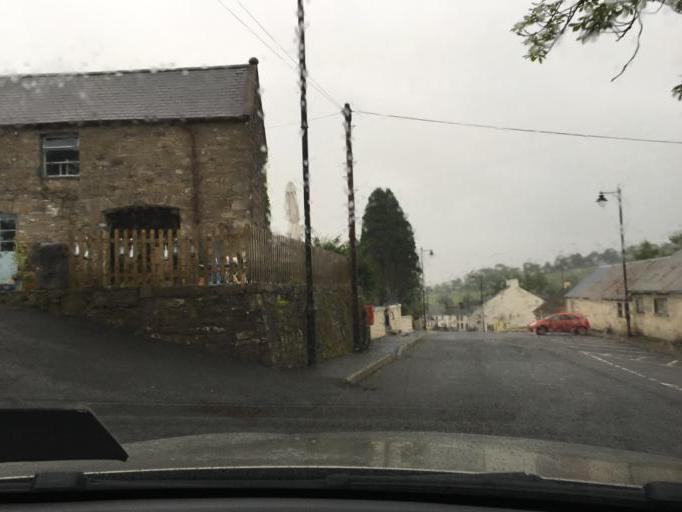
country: GB
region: Northern Ireland
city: Irvinestown
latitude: 54.5502
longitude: -7.8309
